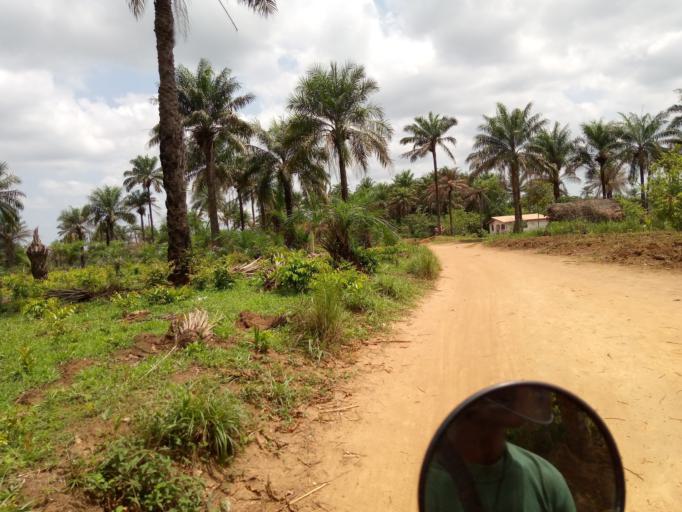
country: SL
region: Western Area
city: Waterloo
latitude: 8.3998
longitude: -12.9476
